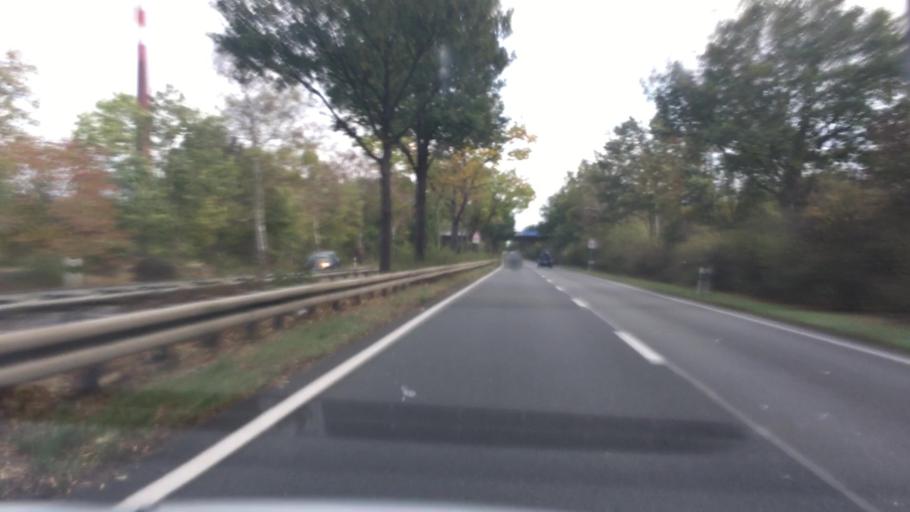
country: DE
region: Lower Saxony
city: Neustadt am Rubenberge
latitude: 52.4812
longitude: 9.5011
